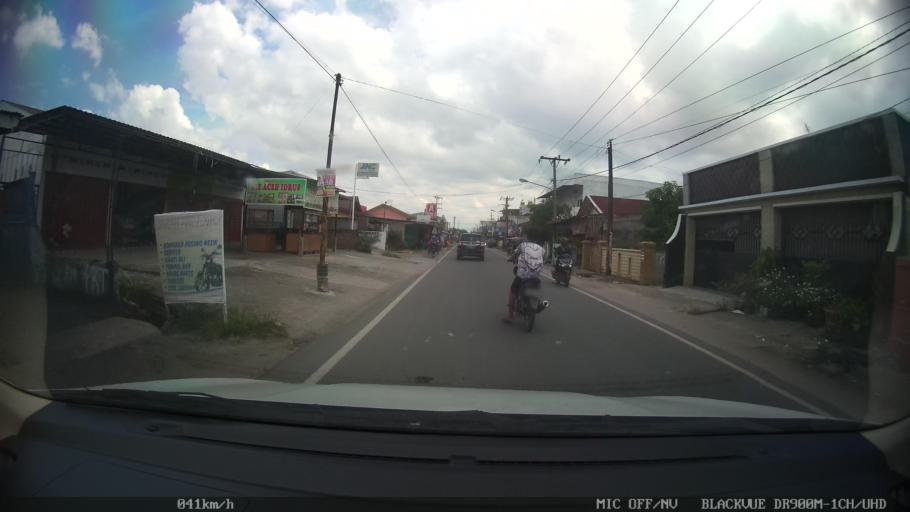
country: ID
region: North Sumatra
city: Sunggal
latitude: 3.6156
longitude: 98.6240
